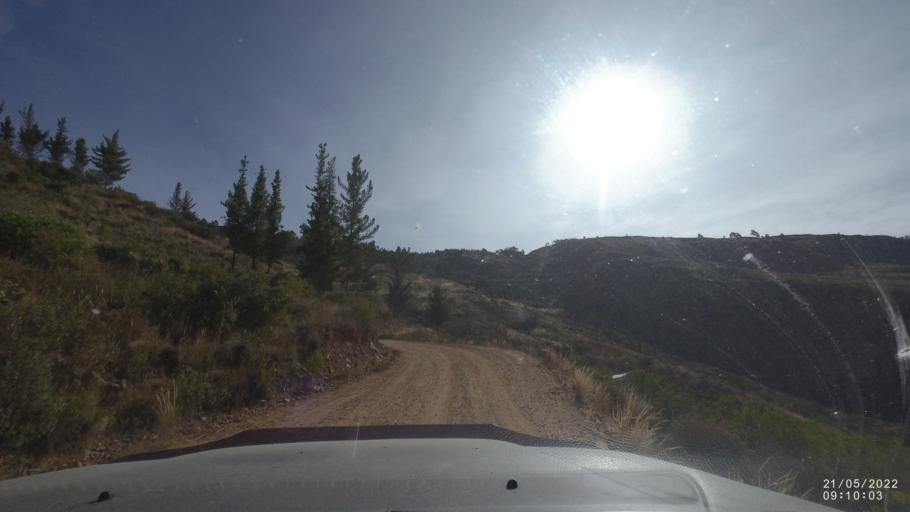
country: BO
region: Cochabamba
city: Cochabamba
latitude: -17.3733
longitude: -66.0225
